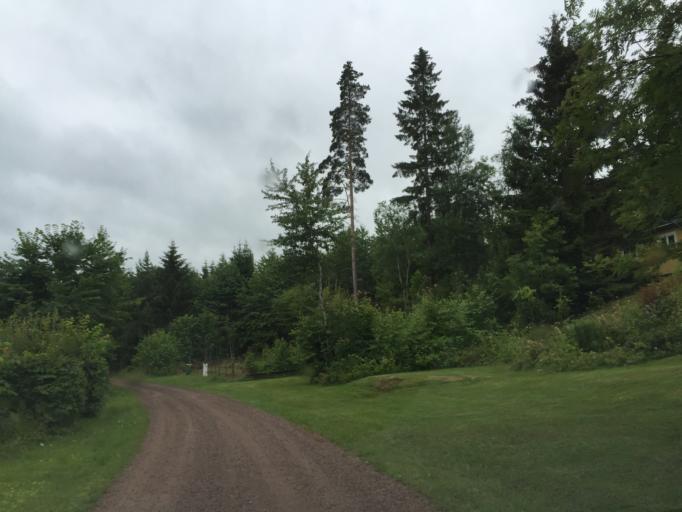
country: SE
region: OEstergoetland
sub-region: Vadstena Kommun
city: Vadstena
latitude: 58.4758
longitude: 14.8294
